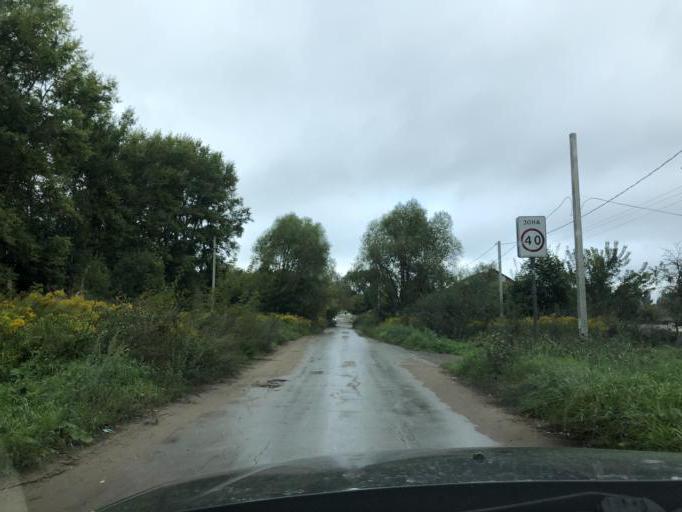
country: RU
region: Tula
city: Mendeleyevskiy
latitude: 54.1731
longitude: 37.5525
